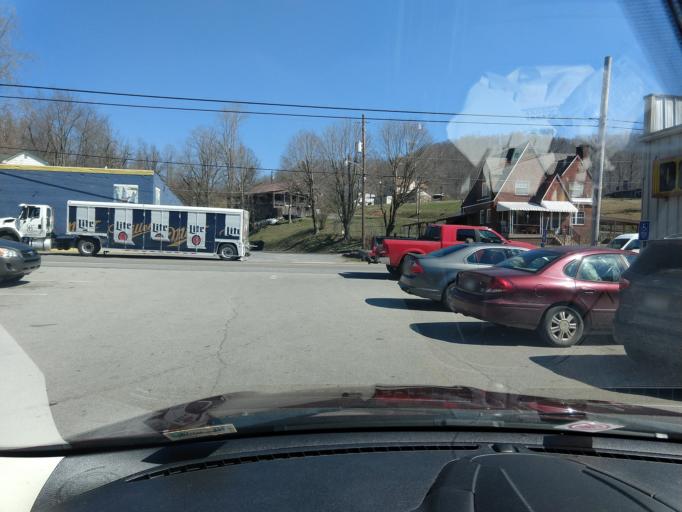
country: US
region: West Virginia
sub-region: Braxton County
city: Sutton
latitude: 38.6699
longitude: -80.7194
